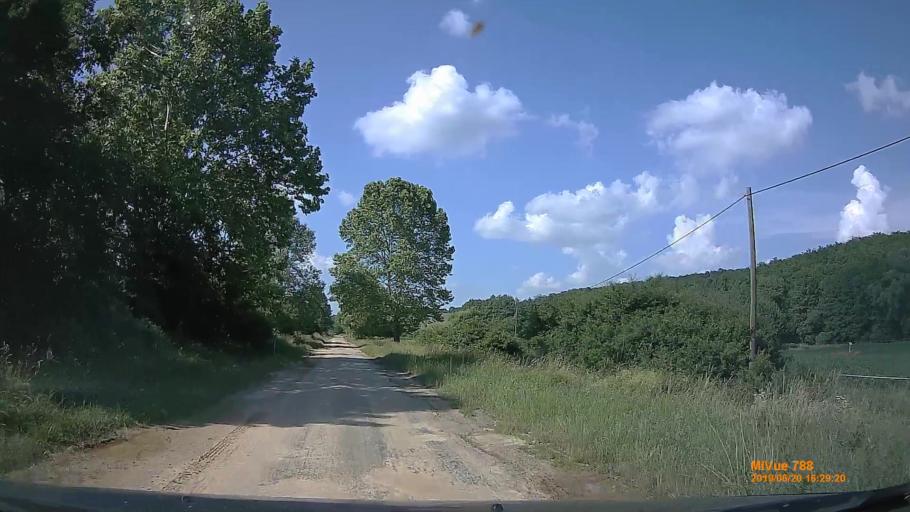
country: HU
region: Baranya
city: Buekkoesd
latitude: 46.1604
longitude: 18.0584
